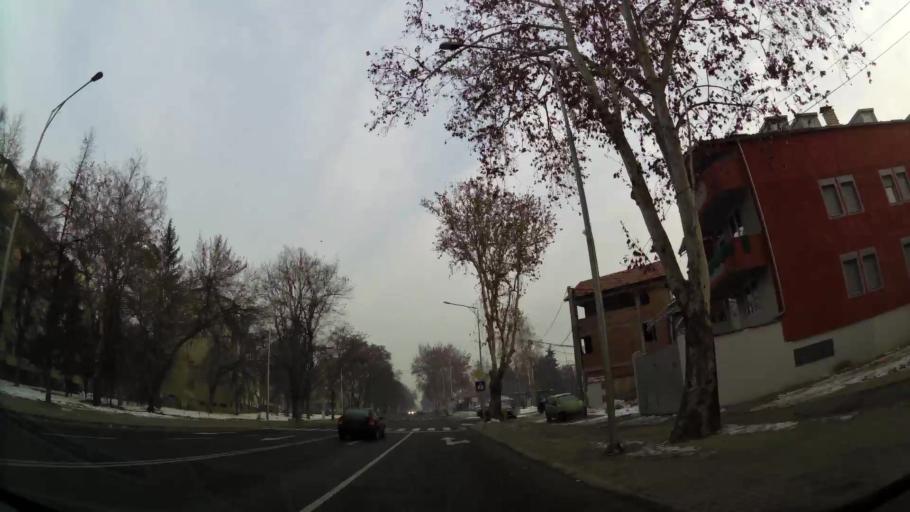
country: MK
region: Cair
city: Cair
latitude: 42.0161
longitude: 21.4469
